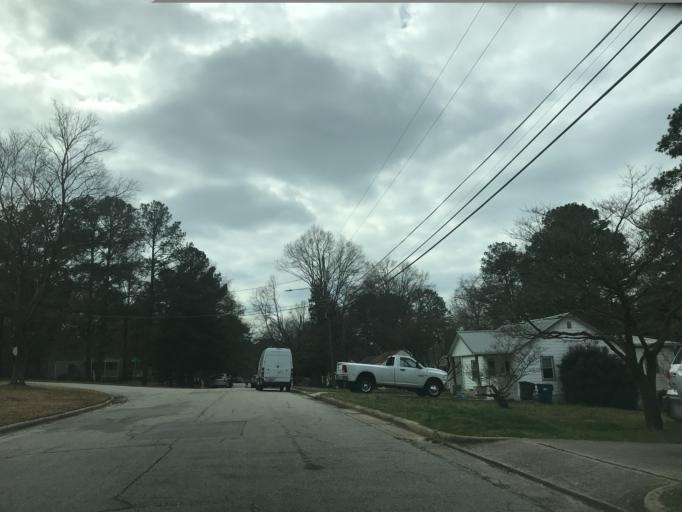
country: US
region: North Carolina
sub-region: Wake County
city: Raleigh
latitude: 35.8006
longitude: -78.6219
